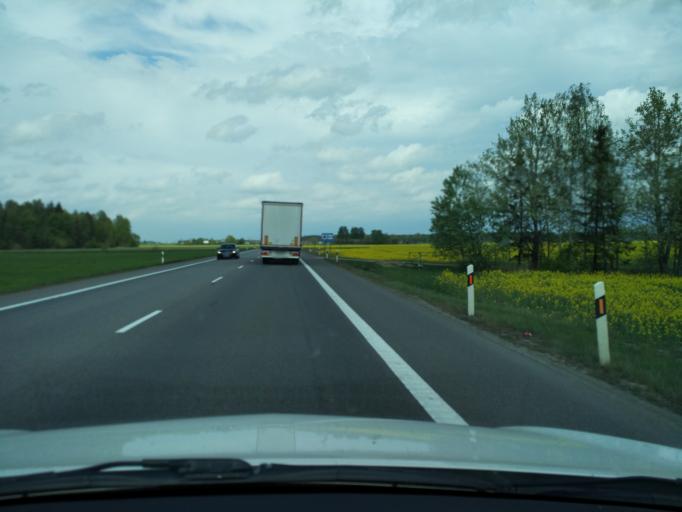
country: LT
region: Panevezys
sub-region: Panevezys City
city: Panevezys
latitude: 55.8198
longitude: 24.3674
